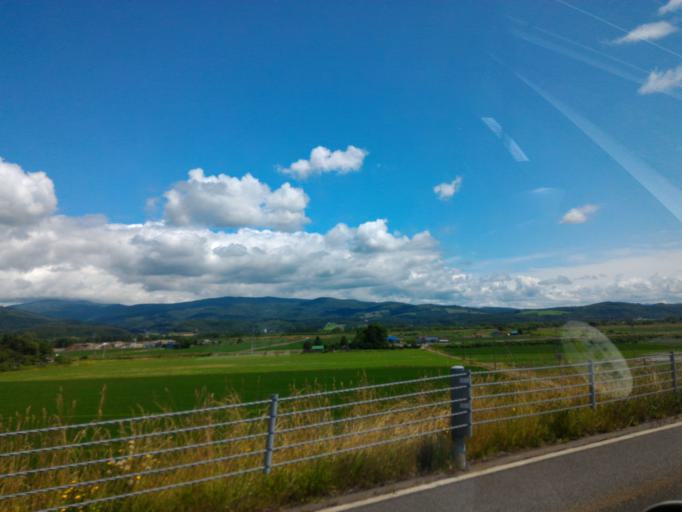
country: JP
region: Hokkaido
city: Nayoro
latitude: 44.3743
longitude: 142.4313
